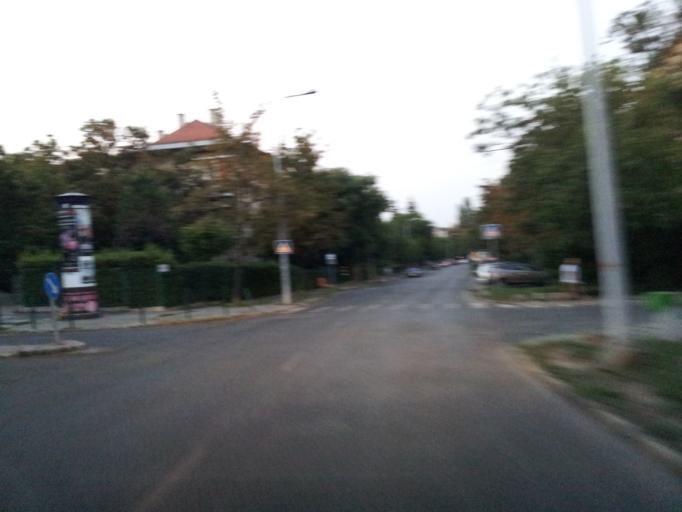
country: HU
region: Budapest
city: Budapest XII. keruelet
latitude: 47.4949
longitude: 19.0149
